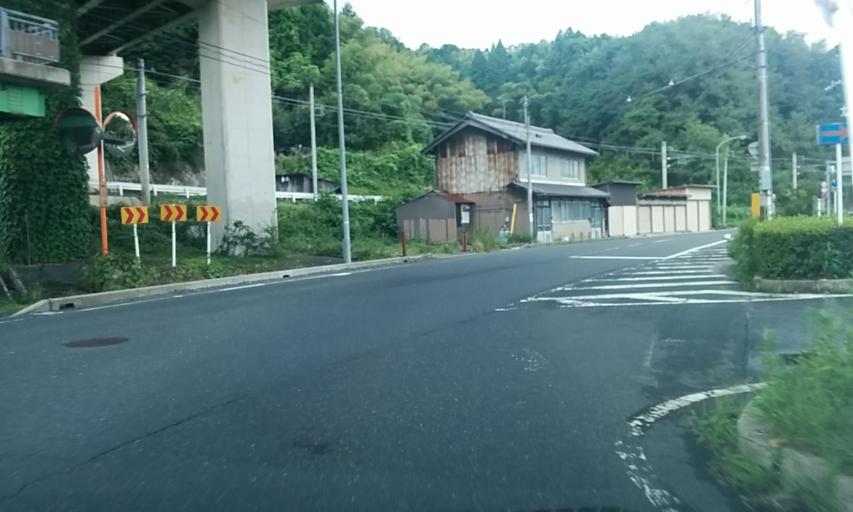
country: JP
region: Kyoto
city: Miyazu
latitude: 35.5472
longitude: 135.1871
